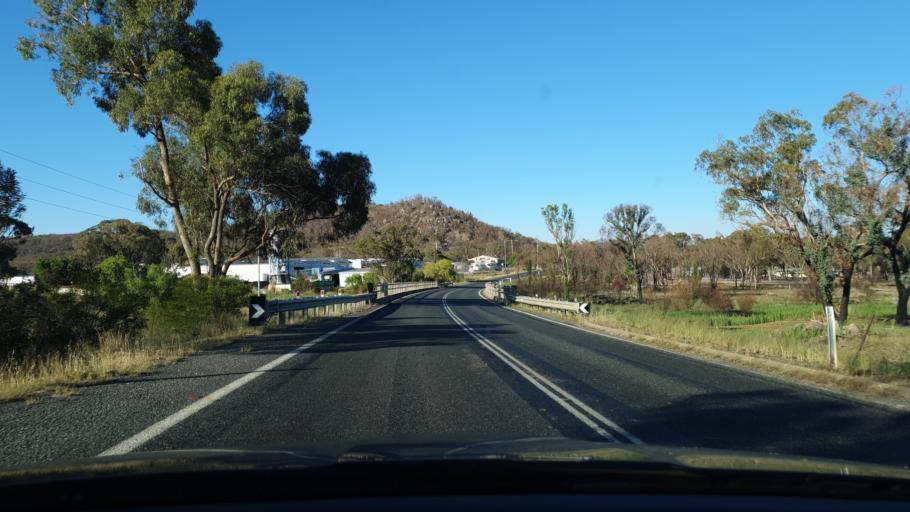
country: AU
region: Queensland
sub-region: Southern Downs
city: Stanthorpe
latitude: -28.6541
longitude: 151.9179
